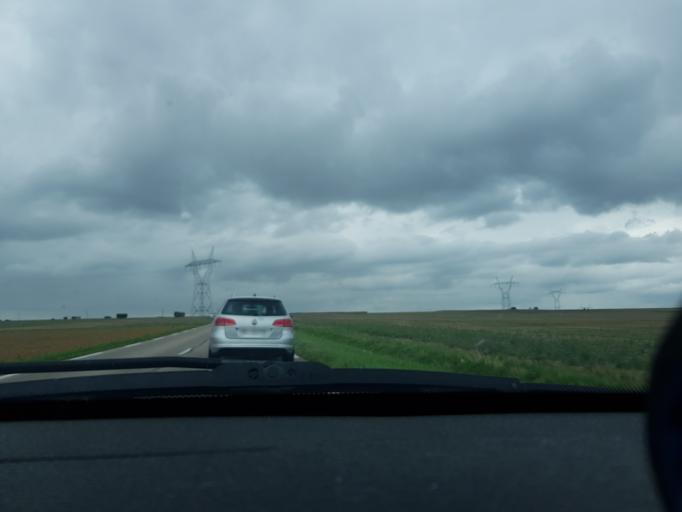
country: FR
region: Lorraine
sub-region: Departement de la Moselle
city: Faulquemont
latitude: 48.9913
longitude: 6.5998
